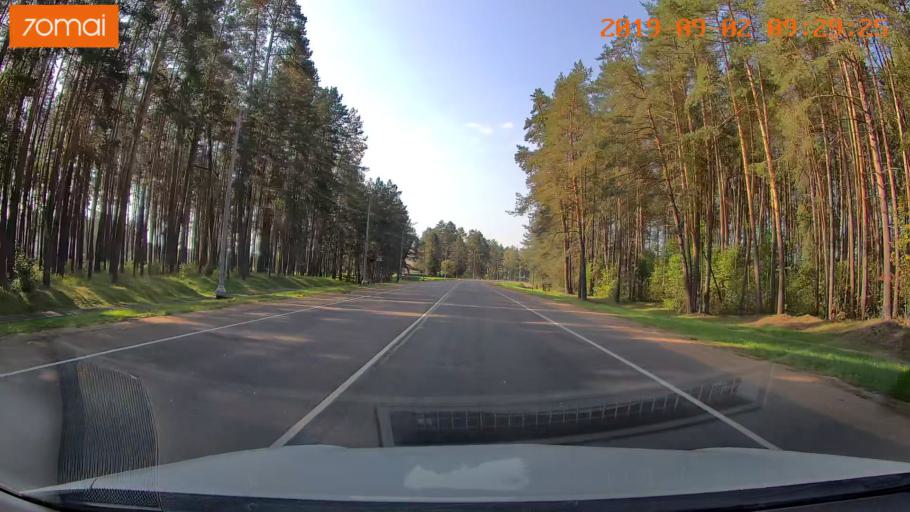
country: RU
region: Kaluga
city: Yukhnov
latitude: 54.7414
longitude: 35.2143
